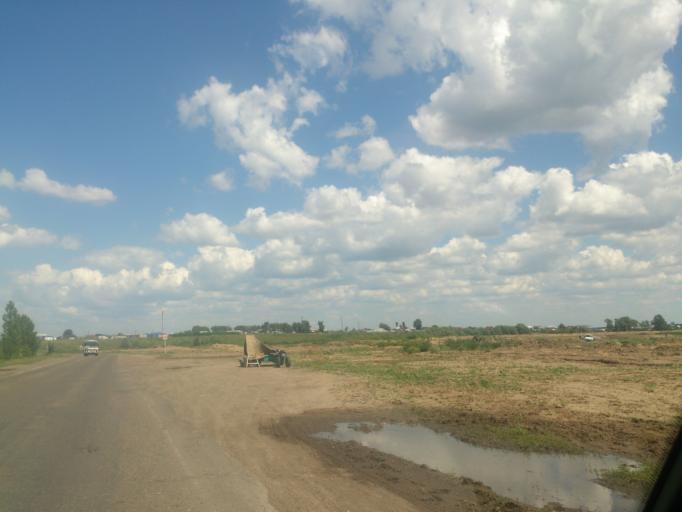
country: RU
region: Ulyanovsk
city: Cherdakly
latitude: 54.4340
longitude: 48.9034
